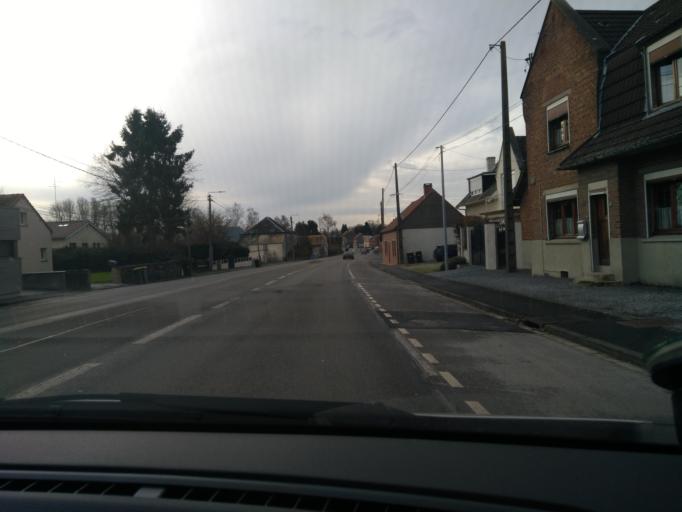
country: FR
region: Nord-Pas-de-Calais
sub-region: Departement du Nord
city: Maubeuge
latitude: 50.3111
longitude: 3.9774
